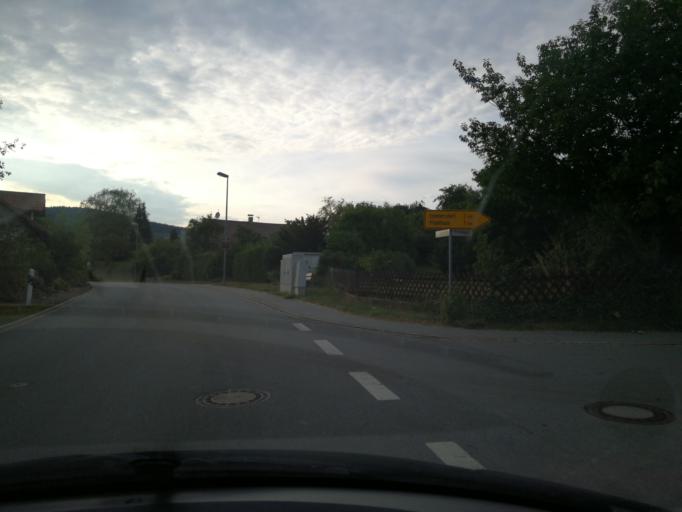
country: DE
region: Bavaria
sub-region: Lower Bavaria
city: Rattiszell
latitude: 49.0370
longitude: 12.6329
